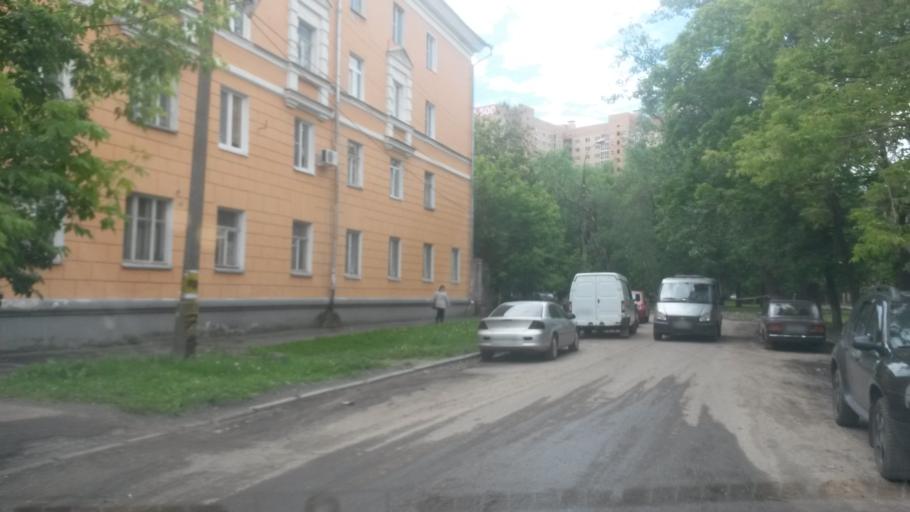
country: RU
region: Jaroslavl
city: Yaroslavl
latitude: 57.6423
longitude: 39.8743
